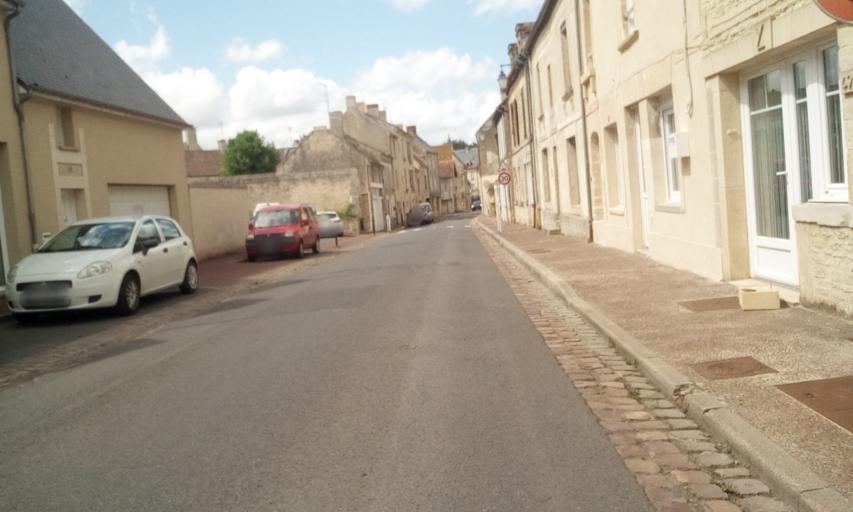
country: FR
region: Lower Normandy
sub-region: Departement du Calvados
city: Creully
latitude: 49.2850
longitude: -0.5359
